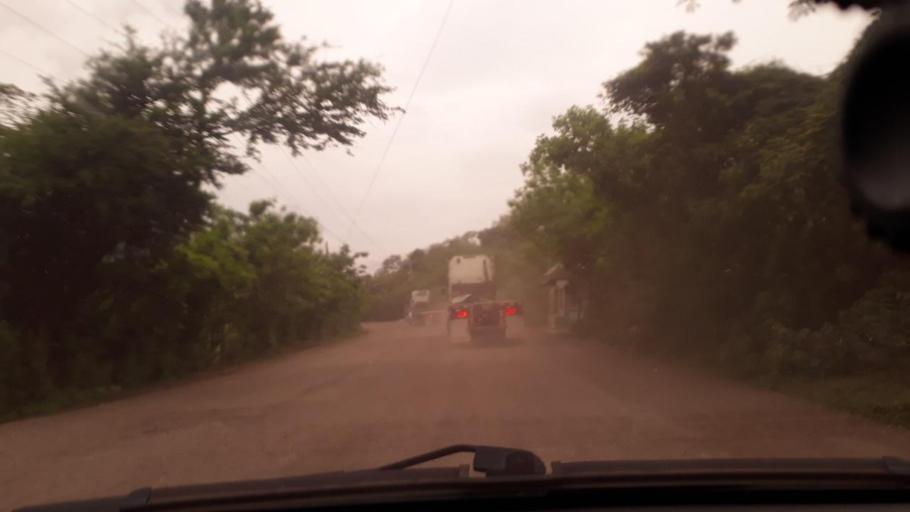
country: GT
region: Chiquimula
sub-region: Municipio de San Juan Ermita
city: San Juan Ermita
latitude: 14.7723
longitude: -89.4226
